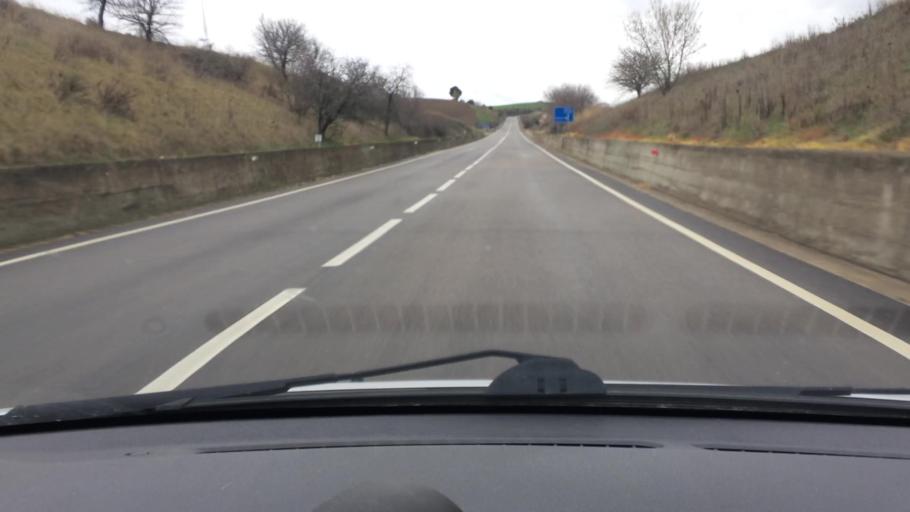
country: IT
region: Basilicate
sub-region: Provincia di Potenza
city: San Chirico Nuovo
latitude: 40.7677
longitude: 16.1059
